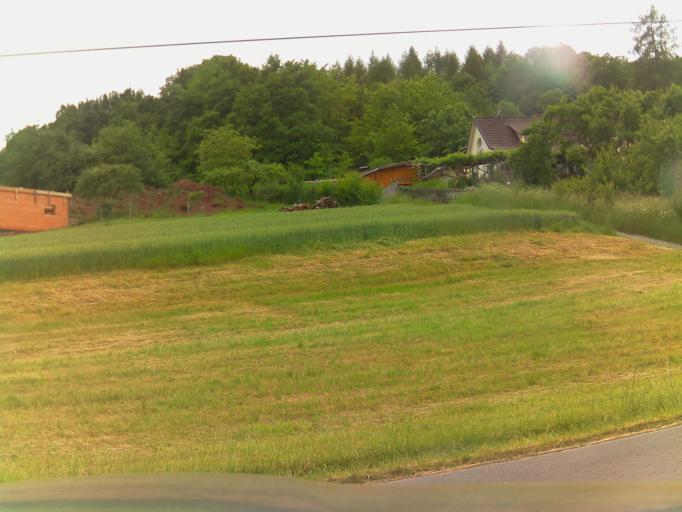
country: DE
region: Bavaria
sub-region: Regierungsbezirk Unterfranken
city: Oberelsbach
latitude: 50.4413
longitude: 10.1121
